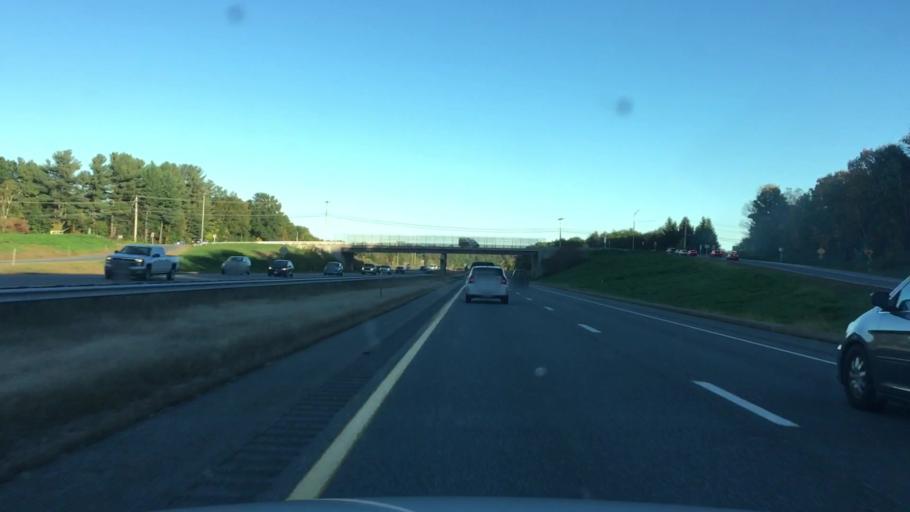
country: US
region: New Hampshire
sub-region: Rockingham County
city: Exeter
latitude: 43.0018
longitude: -70.9497
